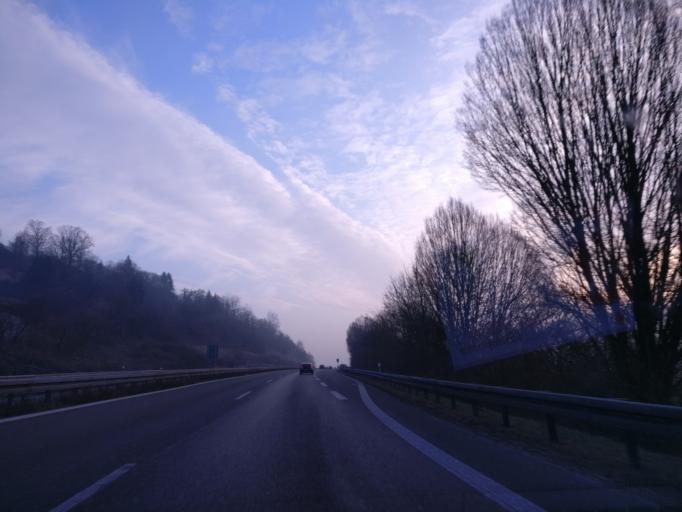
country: DE
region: Baden-Wuerttemberg
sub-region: Regierungsbezirk Stuttgart
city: Bortlingen
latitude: 48.7883
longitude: 9.6319
